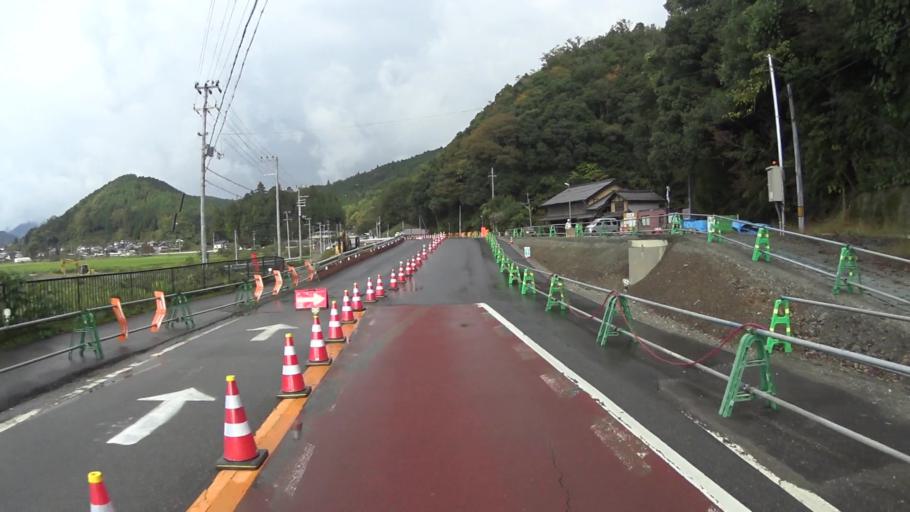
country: JP
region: Kyoto
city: Fukuchiyama
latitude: 35.3934
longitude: 135.1756
